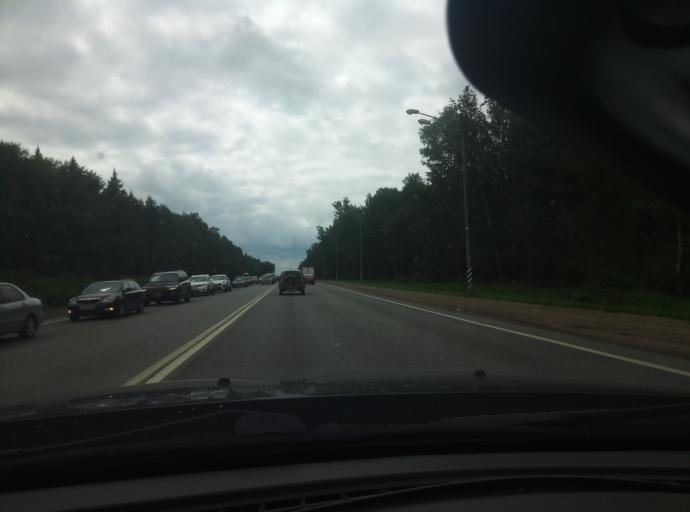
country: RU
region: Kaluga
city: Obninsk
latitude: 55.0854
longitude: 36.6321
